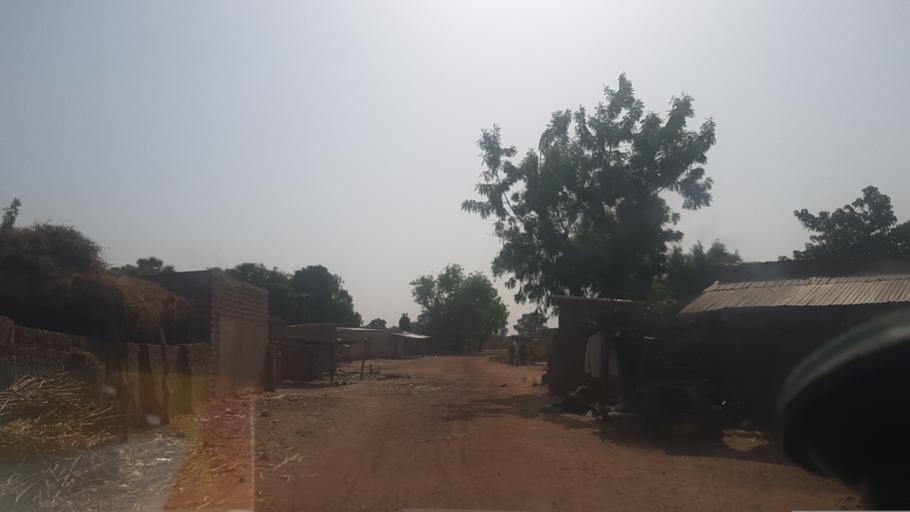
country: ML
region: Segou
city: Baroueli
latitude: 13.1660
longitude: -6.5195
